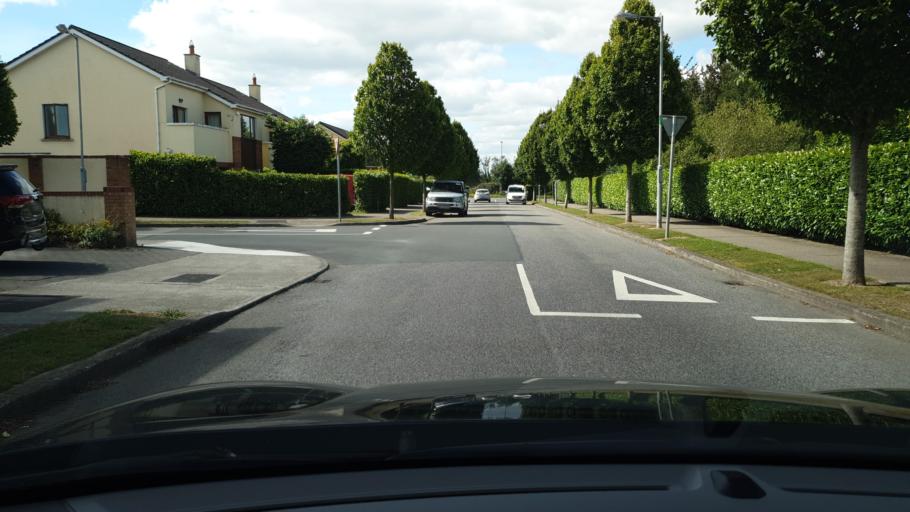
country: IE
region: Leinster
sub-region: An Mhi
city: Dunboyne
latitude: 53.4145
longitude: -6.4822
